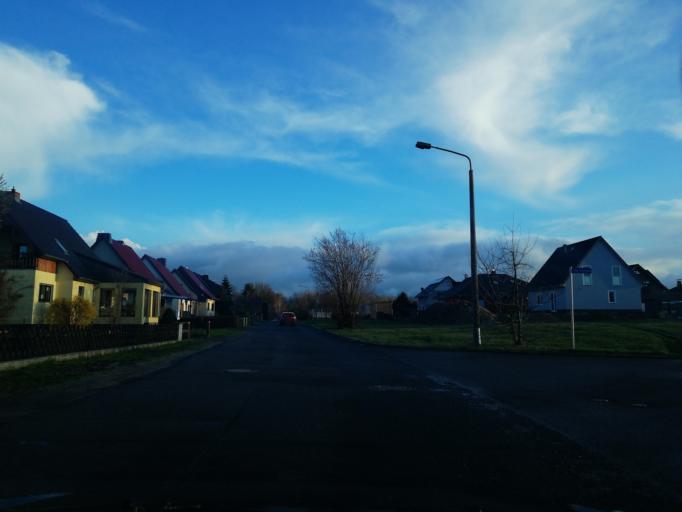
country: DE
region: Brandenburg
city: Calau
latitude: 51.7384
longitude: 13.9648
